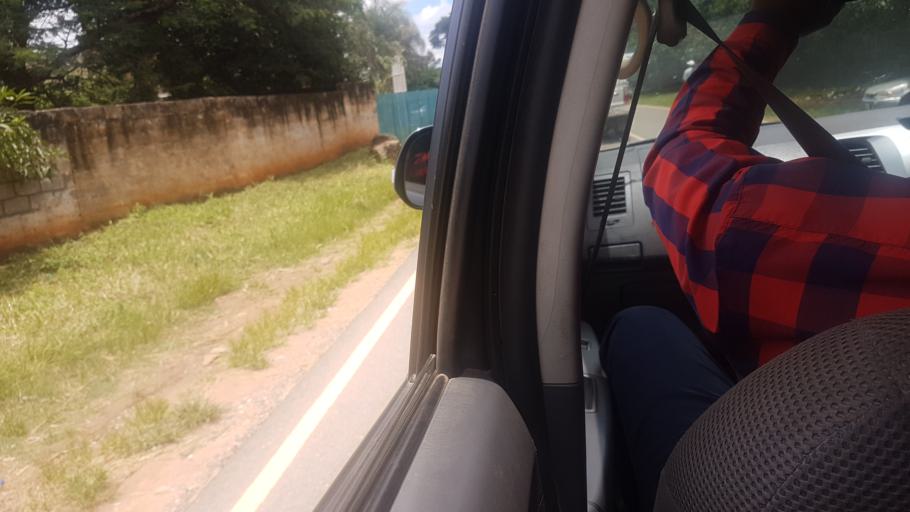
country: ZM
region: Lusaka
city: Lusaka
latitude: -15.4289
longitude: 28.3100
